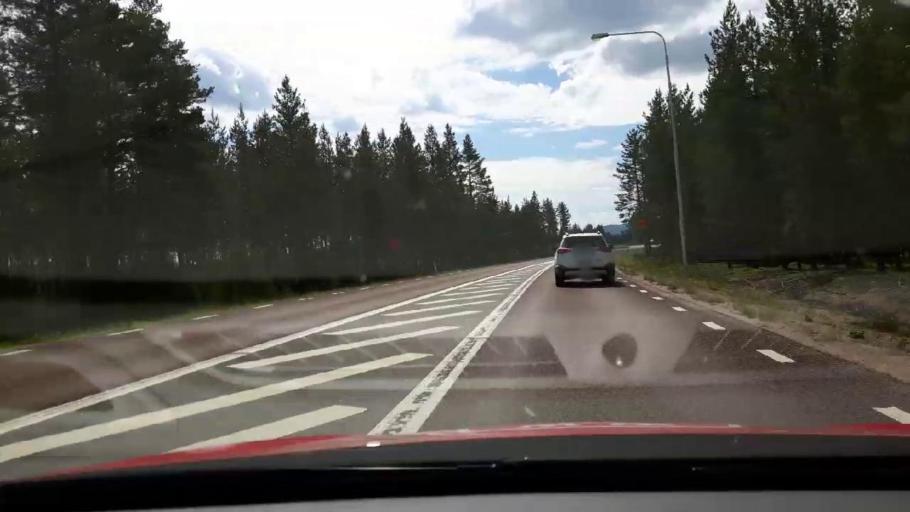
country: SE
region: Jaemtland
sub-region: Harjedalens Kommun
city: Sveg
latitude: 62.1287
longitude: 14.9720
